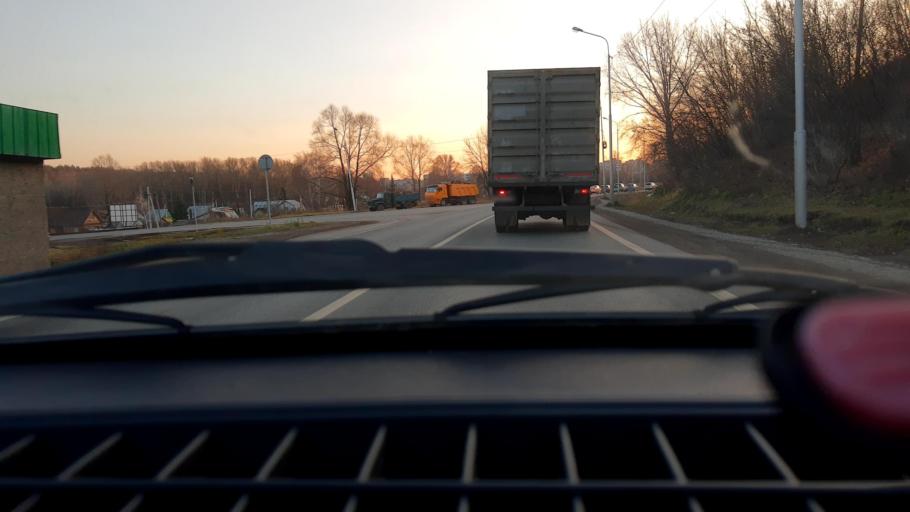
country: RU
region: Bashkortostan
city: Ufa
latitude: 54.8320
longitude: 56.1330
